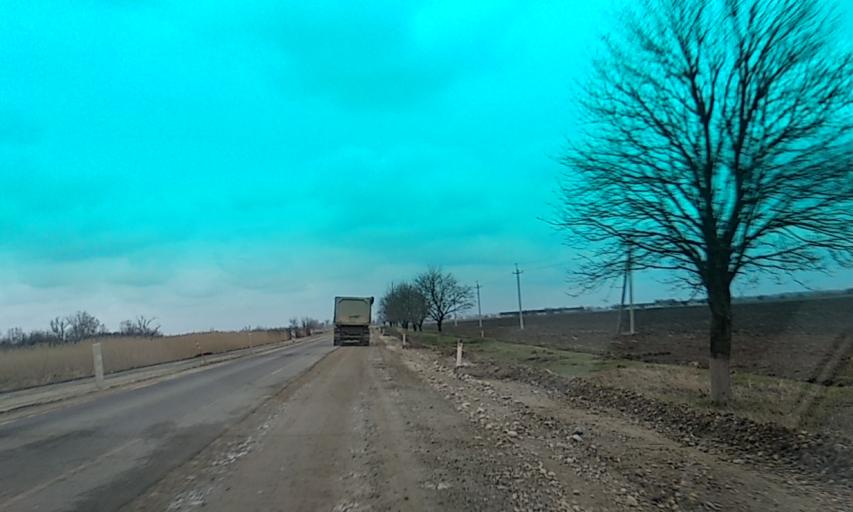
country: RU
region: Krasnodarskiy
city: Velikovechnoye
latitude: 44.9940
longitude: 39.7122
